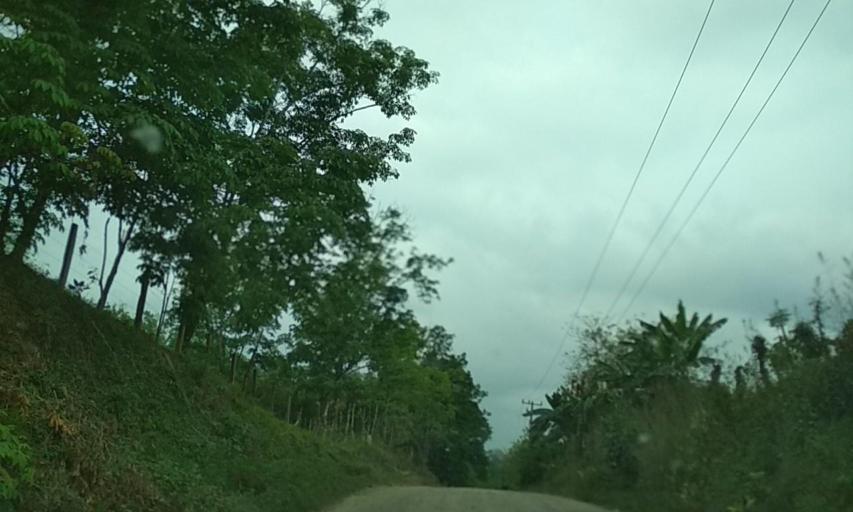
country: MX
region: Veracruz
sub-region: Uxpanapa
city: Poblado 10
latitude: 17.4892
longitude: -94.1288
